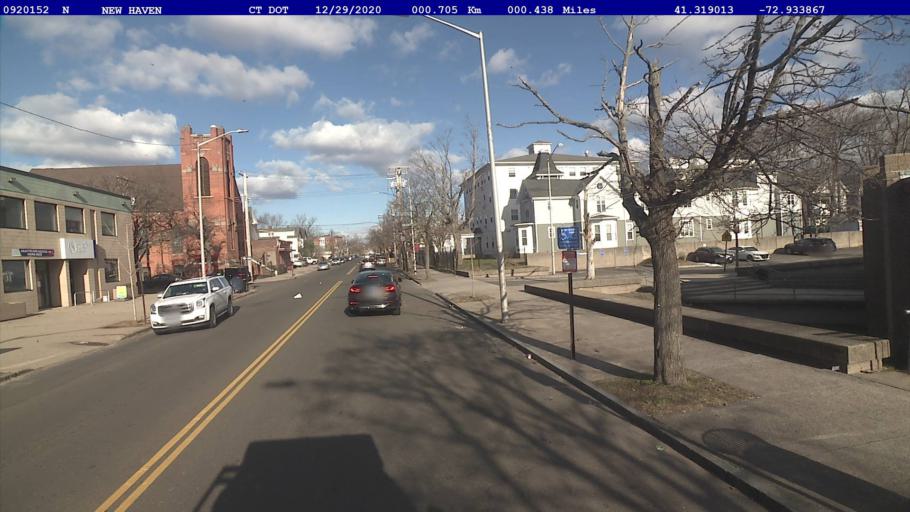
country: US
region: Connecticut
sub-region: New Haven County
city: New Haven
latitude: 41.3190
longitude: -72.9339
